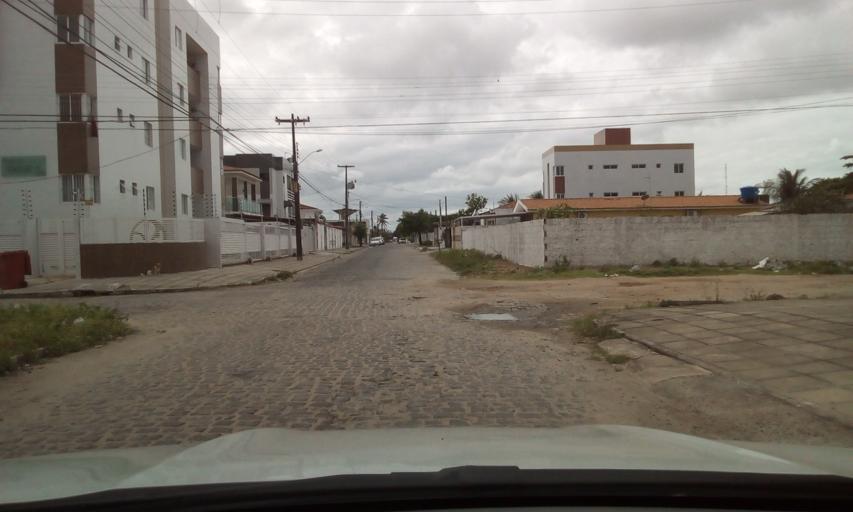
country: BR
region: Paraiba
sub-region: Joao Pessoa
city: Joao Pessoa
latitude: -7.1592
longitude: -34.8686
